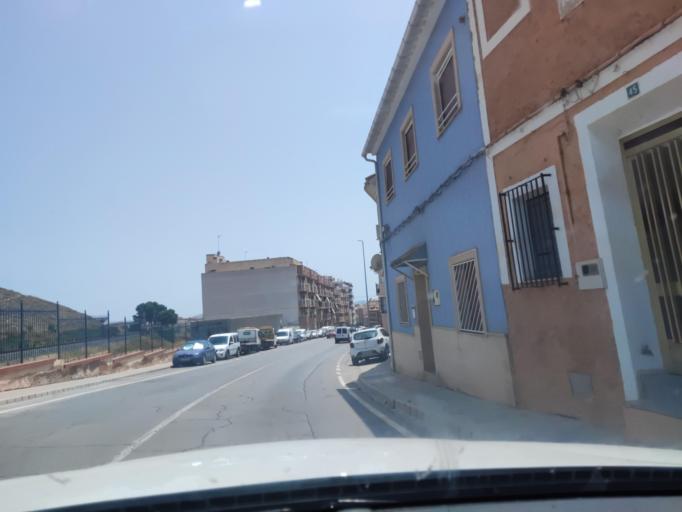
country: ES
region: Castille-La Mancha
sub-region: Provincia de Albacete
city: Hellin
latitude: 38.5151
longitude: -1.6972
